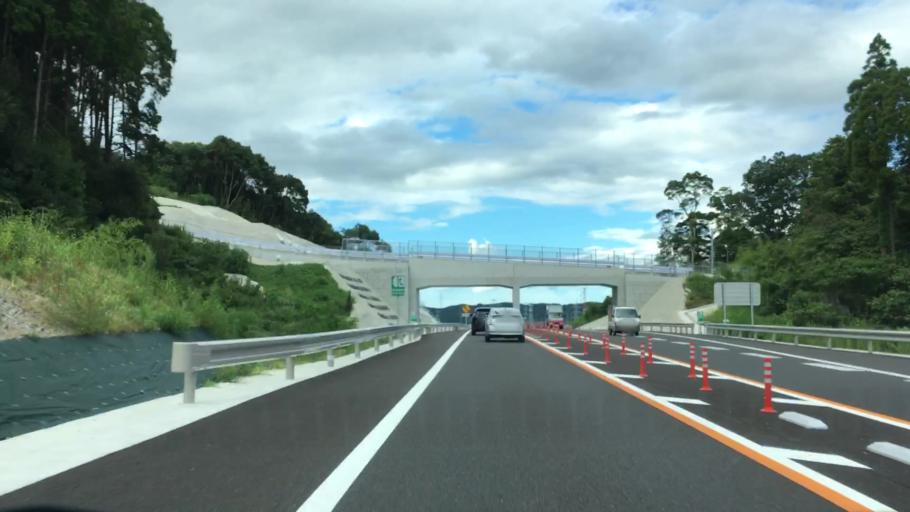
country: JP
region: Saga Prefecture
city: Imaricho-ko
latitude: 33.3310
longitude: 129.9279
